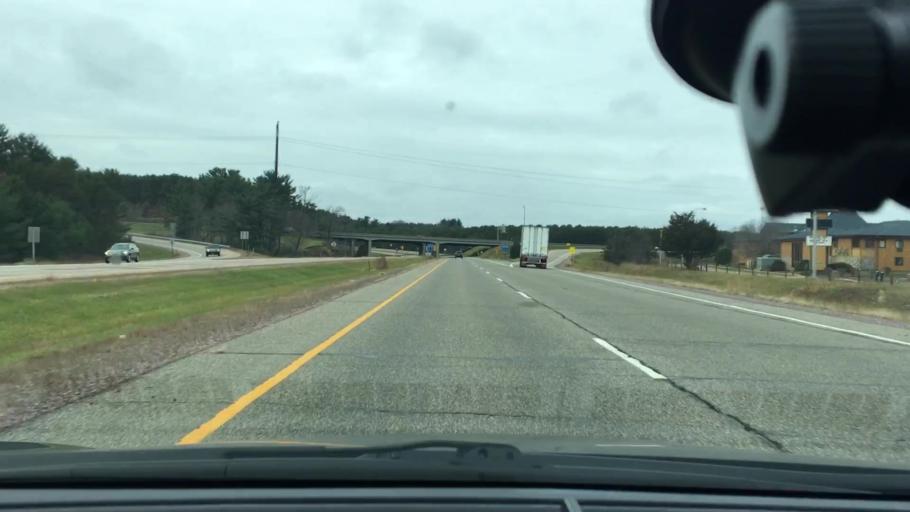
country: US
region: Wisconsin
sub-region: Sauk County
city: Lake Delton
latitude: 43.6244
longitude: -89.7996
